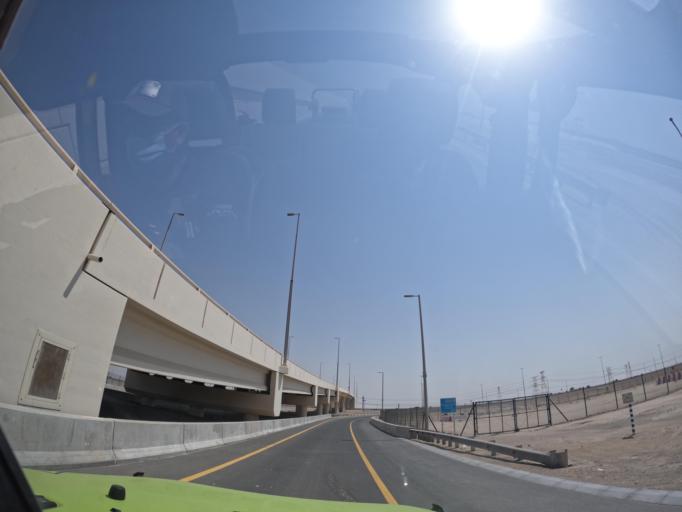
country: AE
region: Abu Dhabi
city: Abu Dhabi
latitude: 24.1648
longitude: 54.3532
